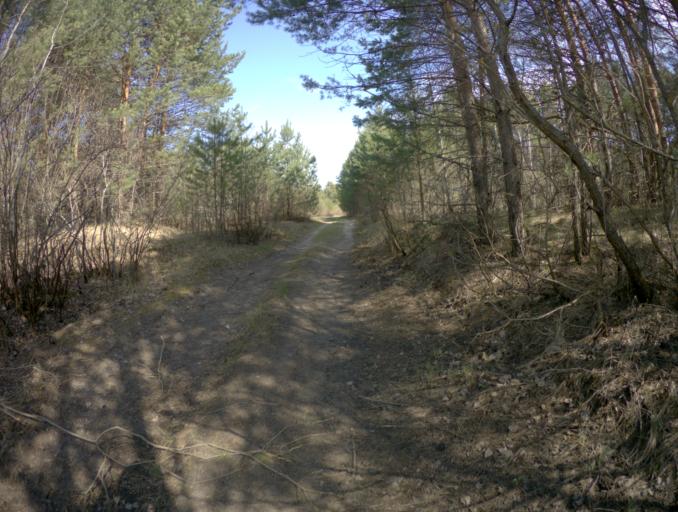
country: RU
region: Vladimir
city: Mezinovskiy
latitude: 55.5420
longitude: 40.2648
